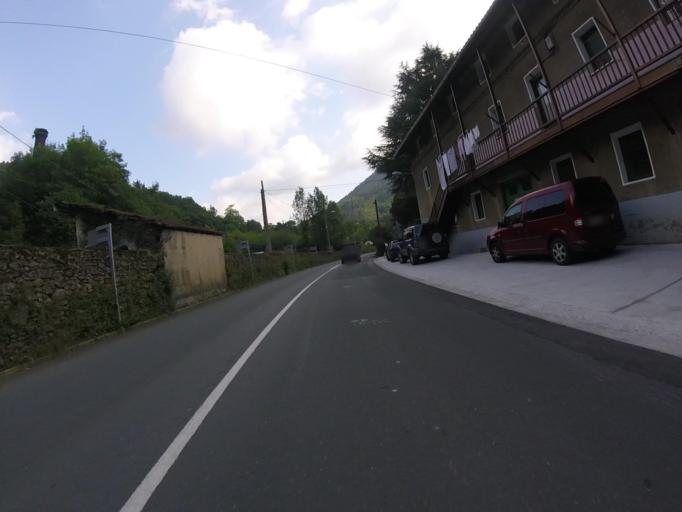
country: ES
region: Basque Country
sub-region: Provincia de Guipuzcoa
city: Astigarraga
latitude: 43.2396
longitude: -1.9336
